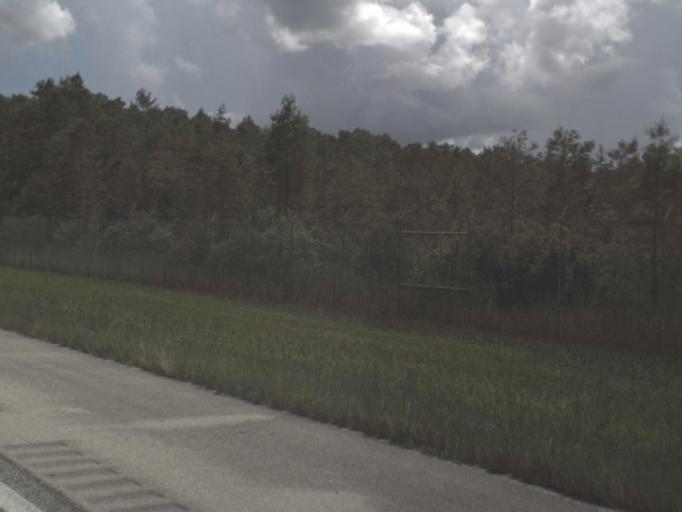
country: US
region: Florida
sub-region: Collier County
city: Immokalee
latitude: 26.1664
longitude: -81.2202
